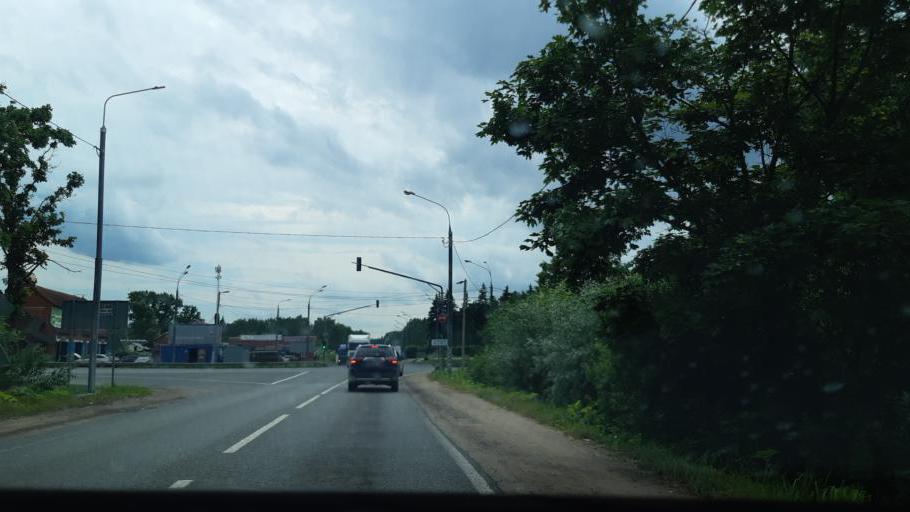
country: RU
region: Moskovskaya
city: Dorokhovo
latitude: 55.5319
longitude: 36.3599
